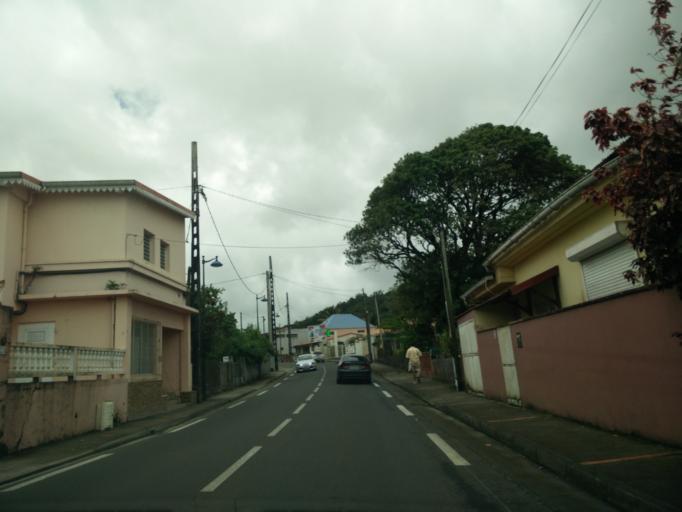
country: MQ
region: Martinique
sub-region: Martinique
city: Le Morne-Rouge
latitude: 14.7708
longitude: -61.1369
